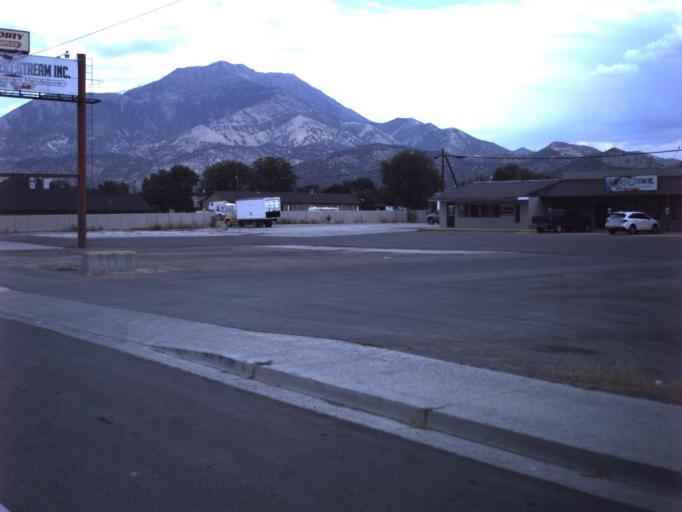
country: US
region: Utah
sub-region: Juab County
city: Nephi
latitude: 39.6964
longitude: -111.8360
